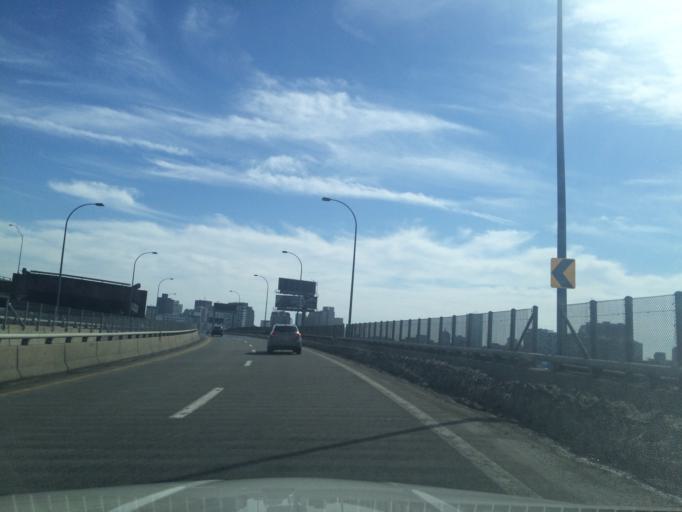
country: US
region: Massachusetts
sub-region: Middlesex County
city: Somerville
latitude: 42.3800
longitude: -71.0776
